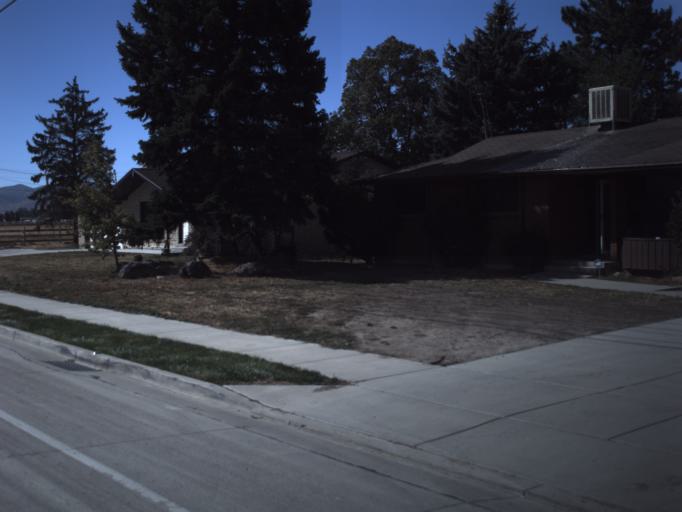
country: US
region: Utah
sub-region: Salt Lake County
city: South Jordan
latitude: 40.5475
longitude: -111.9388
